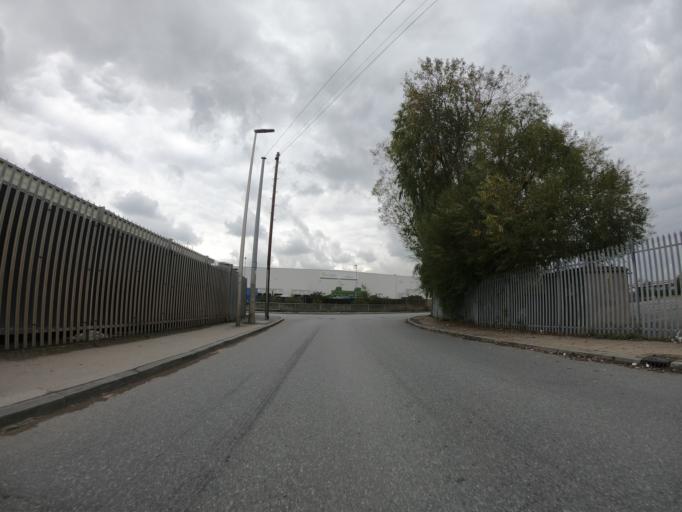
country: GB
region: England
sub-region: Greater London
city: Belvedere
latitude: 51.4969
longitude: 0.1657
